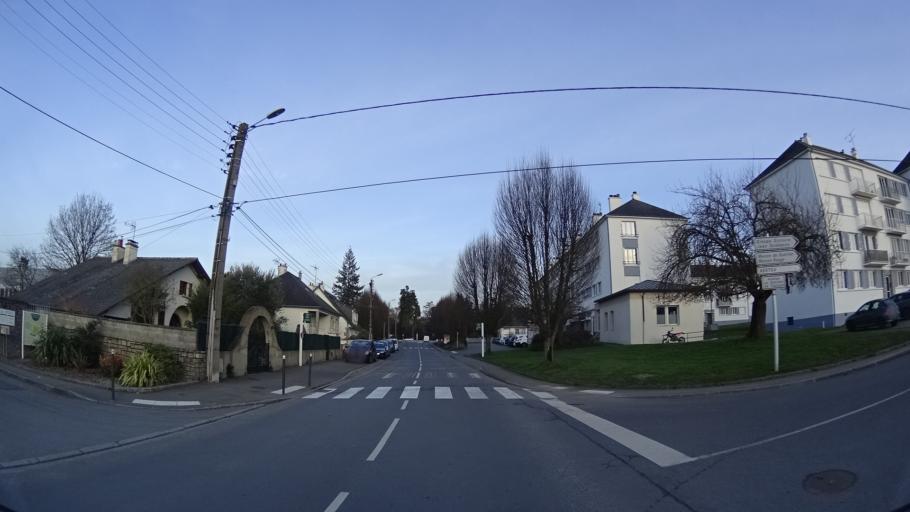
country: FR
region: Brittany
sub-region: Departement d'Ille-et-Vilaine
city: Vitre
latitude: 48.1171
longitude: -1.2127
